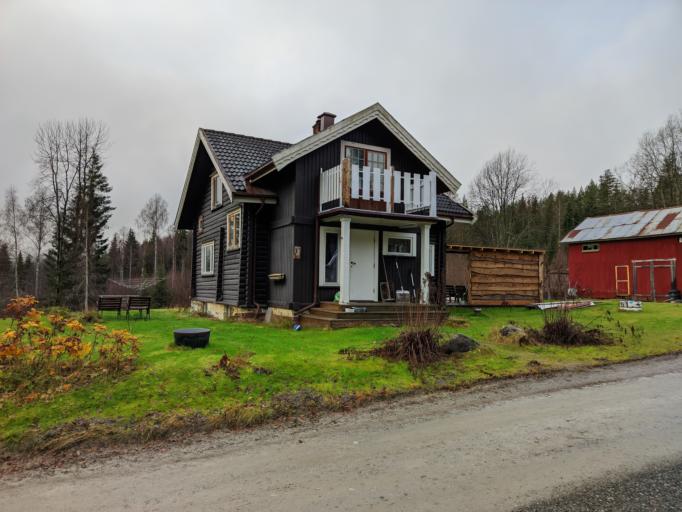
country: NO
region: Buskerud
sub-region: Ringerike
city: Honefoss
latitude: 60.2144
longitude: 10.0228
